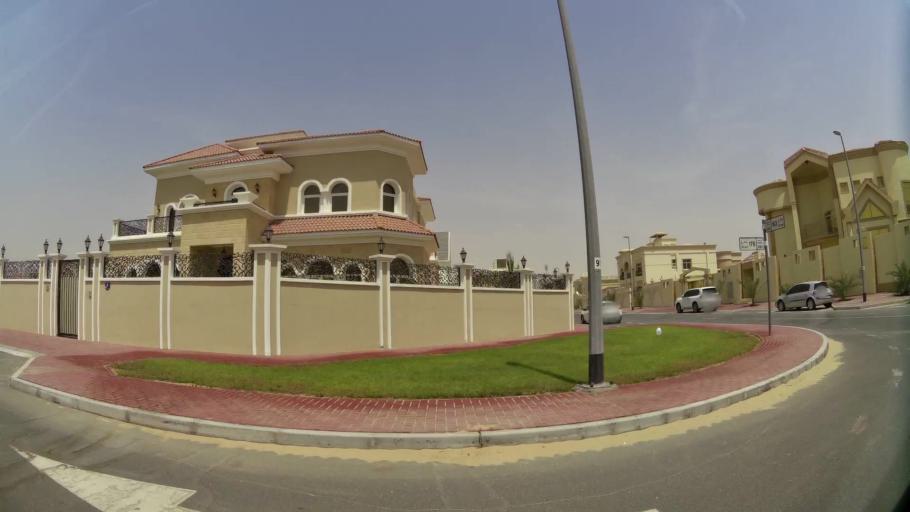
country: AE
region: Ash Shariqah
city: Sharjah
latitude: 25.2511
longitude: 55.5042
